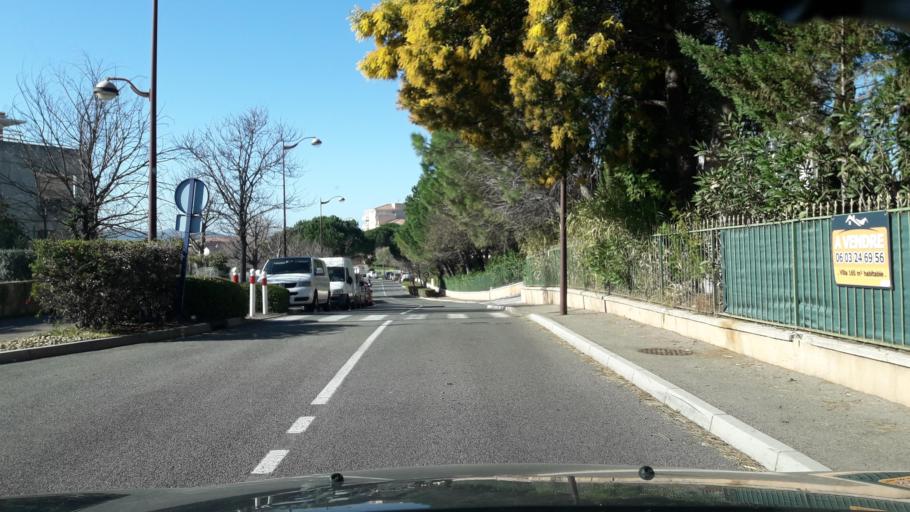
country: FR
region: Provence-Alpes-Cote d'Azur
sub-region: Departement du Var
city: Frejus
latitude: 43.4409
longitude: 6.7508
